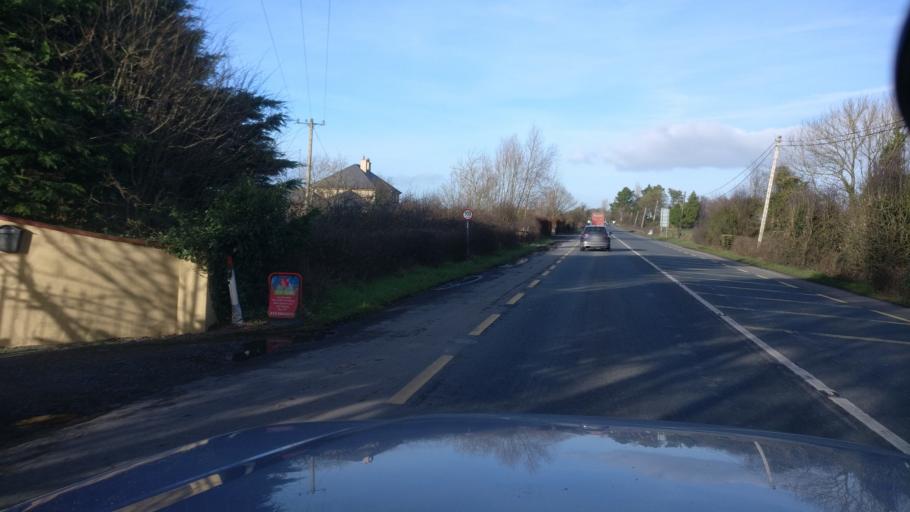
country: IE
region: Leinster
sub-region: Uibh Fhaili
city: Tullamore
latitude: 53.2421
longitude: -7.4780
